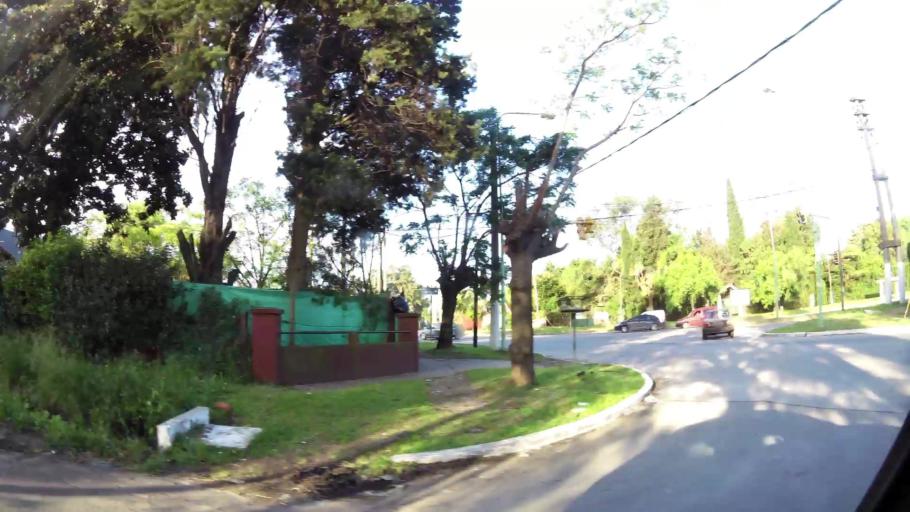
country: AR
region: Buenos Aires
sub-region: Partido de Quilmes
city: Quilmes
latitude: -34.8060
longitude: -58.2067
